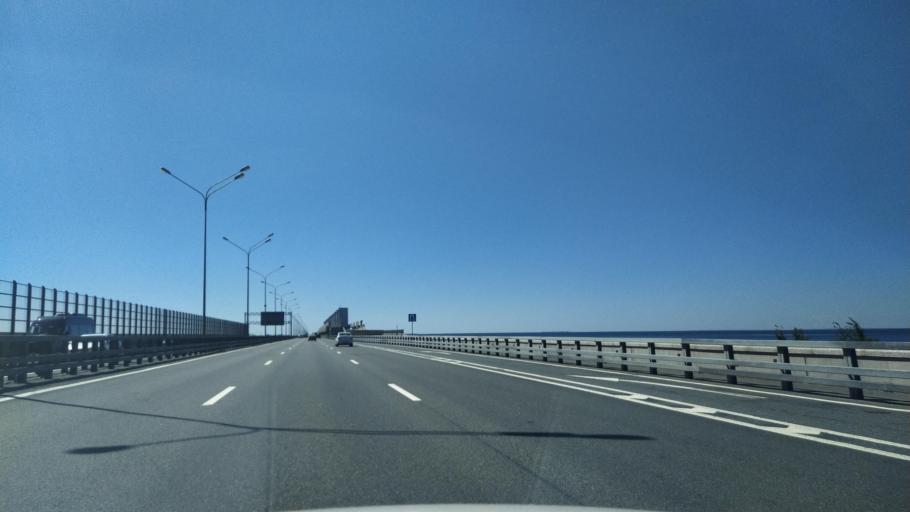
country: RU
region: Leningrad
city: Gorskaya
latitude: 60.0381
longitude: 29.9605
